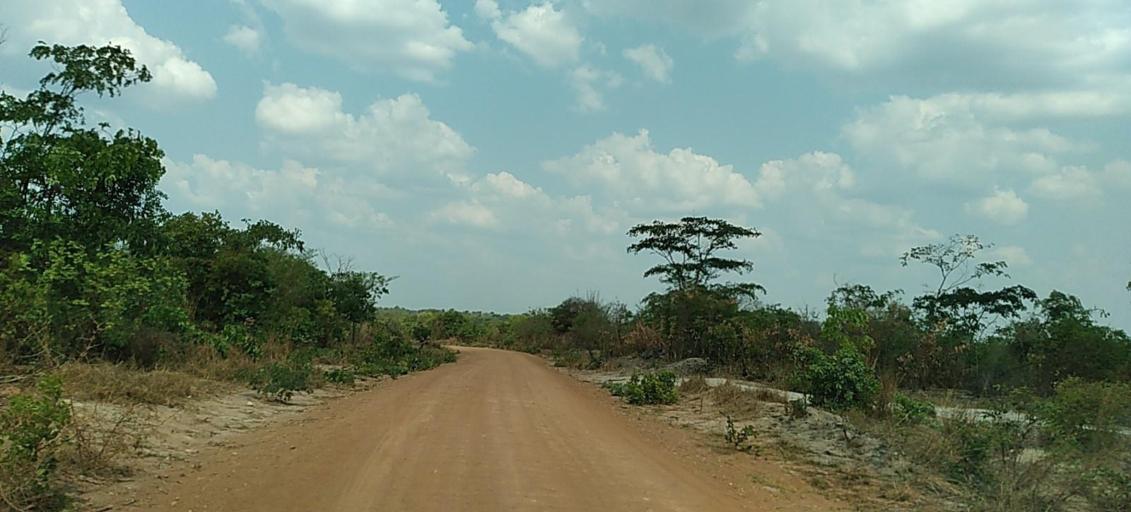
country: ZM
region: Copperbelt
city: Luanshya
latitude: -13.1382
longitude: 28.3392
